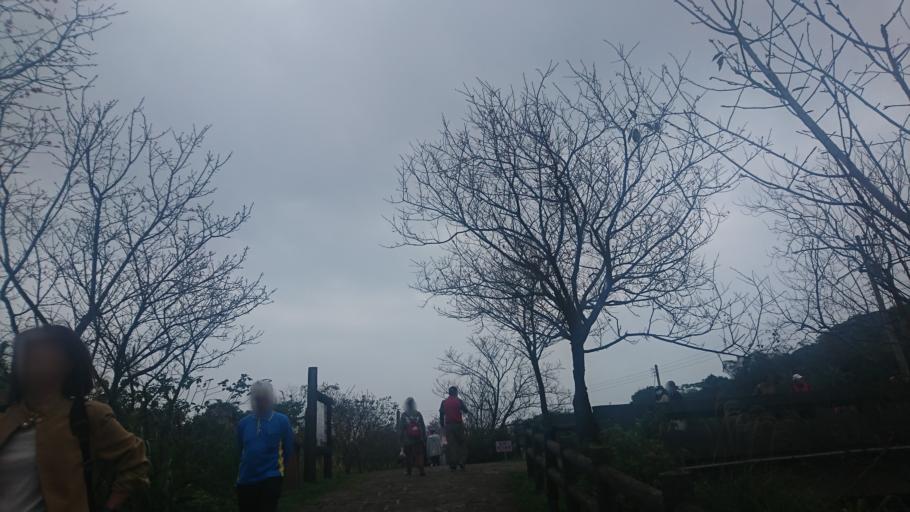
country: TW
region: Taipei
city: Taipei
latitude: 25.2657
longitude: 121.5131
